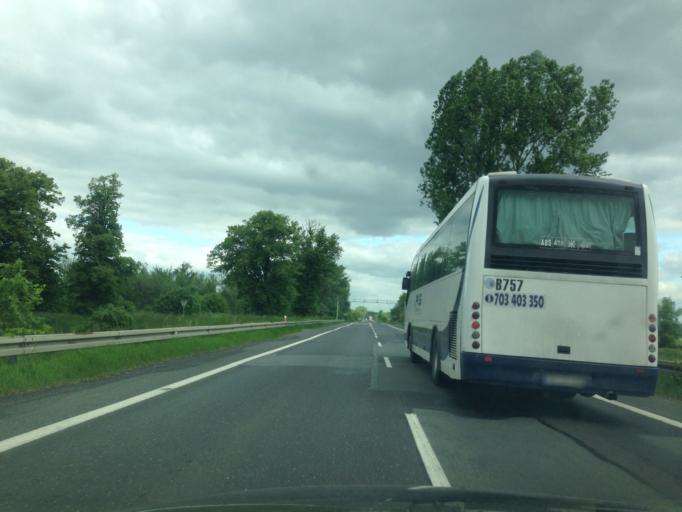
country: PL
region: Kujawsko-Pomorskie
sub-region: Powiat chelminski
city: Chelmno
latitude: 53.3799
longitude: 18.4174
